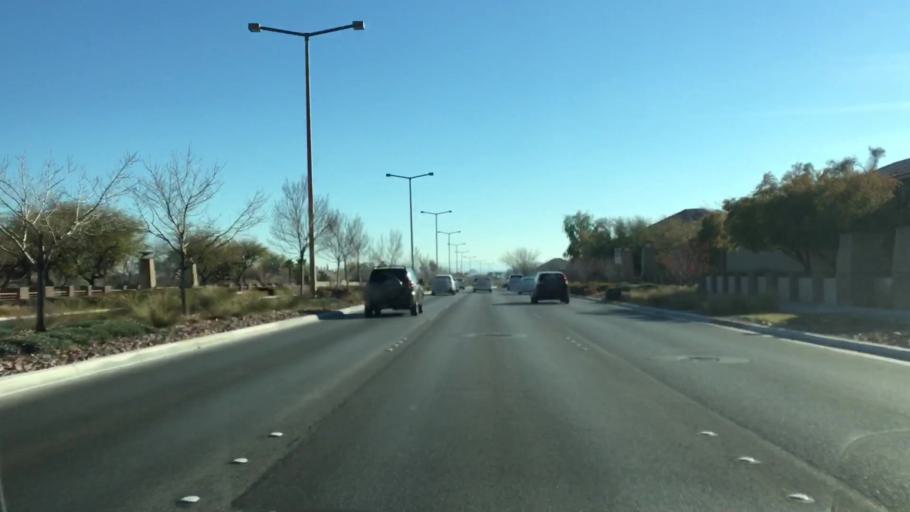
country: US
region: Nevada
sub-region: Clark County
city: Summerlin South
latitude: 36.1379
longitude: -115.3258
